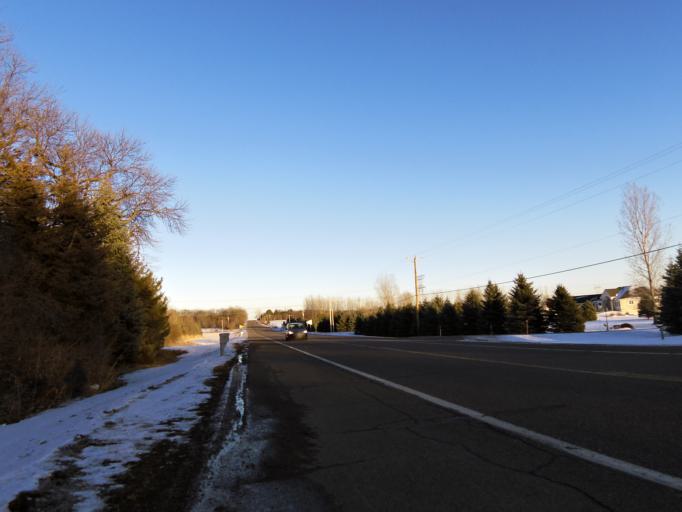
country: US
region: Minnesota
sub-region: Washington County
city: Lakeland
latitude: 44.9634
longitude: -92.8168
